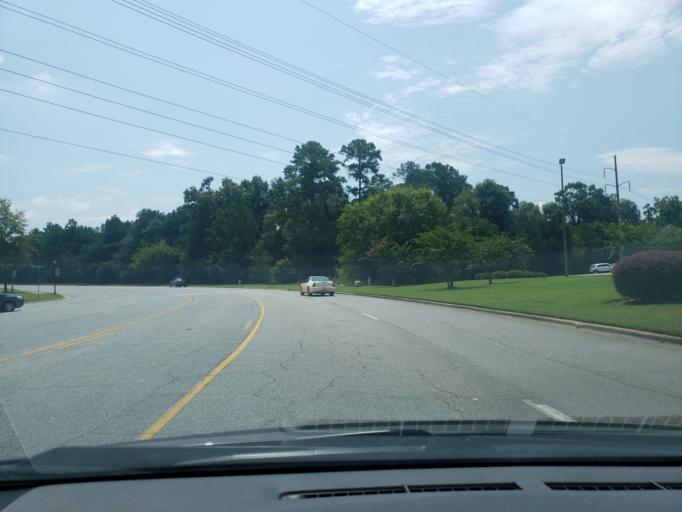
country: US
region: Georgia
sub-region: Dougherty County
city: Albany
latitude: 31.6096
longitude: -84.2193
